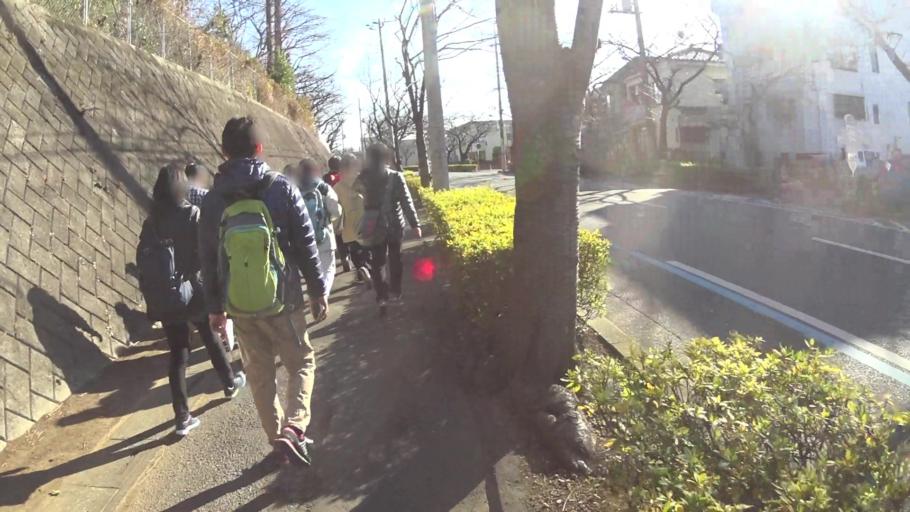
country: JP
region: Saitama
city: Shimotoda
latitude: 35.8421
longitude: 139.6880
